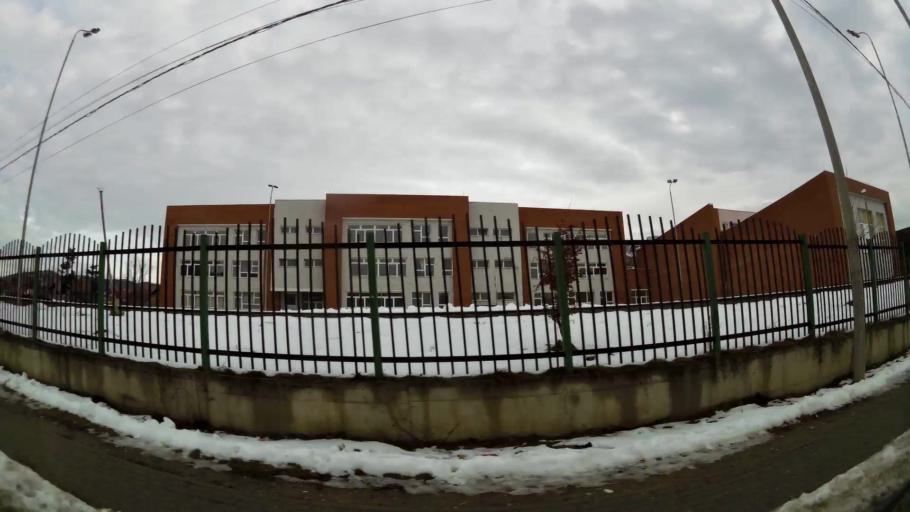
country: XK
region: Pristina
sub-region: Komuna e Prishtines
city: Pristina
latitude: 42.6787
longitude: 21.1729
